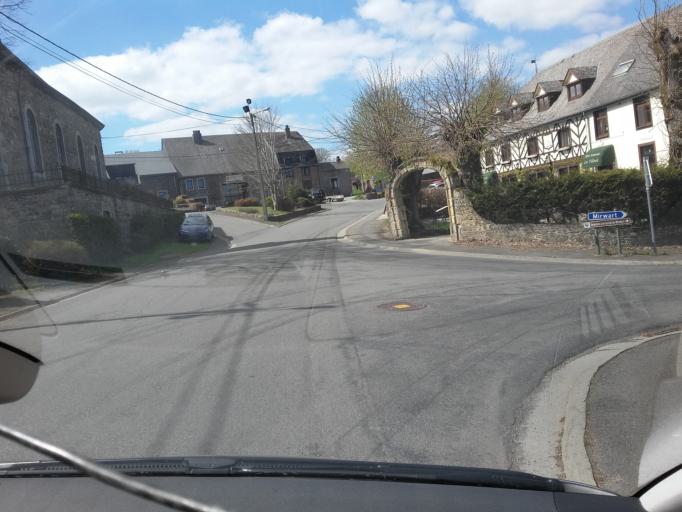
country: BE
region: Wallonia
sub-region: Province du Luxembourg
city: Libin
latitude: 50.0187
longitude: 5.2661
